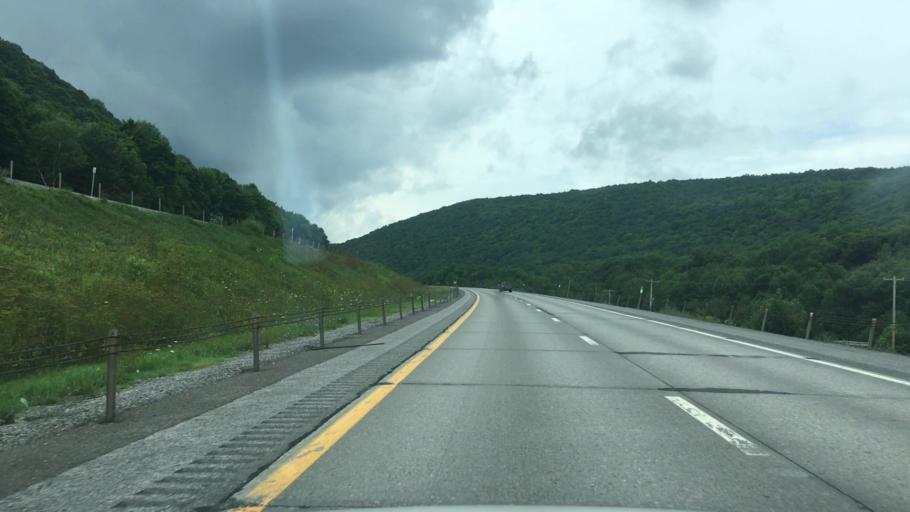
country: US
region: New York
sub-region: Otsego County
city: Worcester
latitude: 42.6491
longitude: -74.6363
